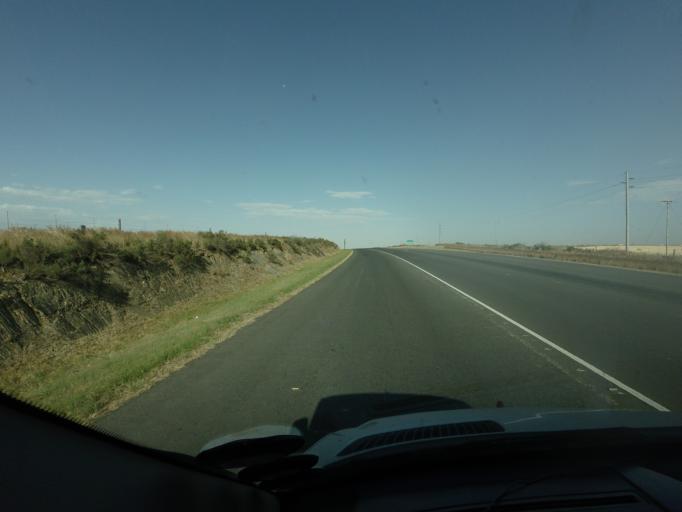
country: ZA
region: Western Cape
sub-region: Cape Winelands District Municipality
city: Ashton
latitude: -34.1583
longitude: 19.9584
